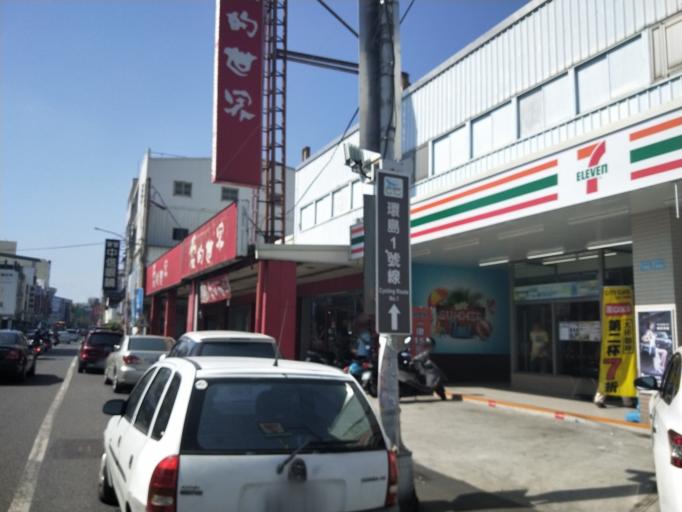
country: TW
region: Taiwan
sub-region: Changhua
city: Chang-hua
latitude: 24.0487
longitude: 120.4417
